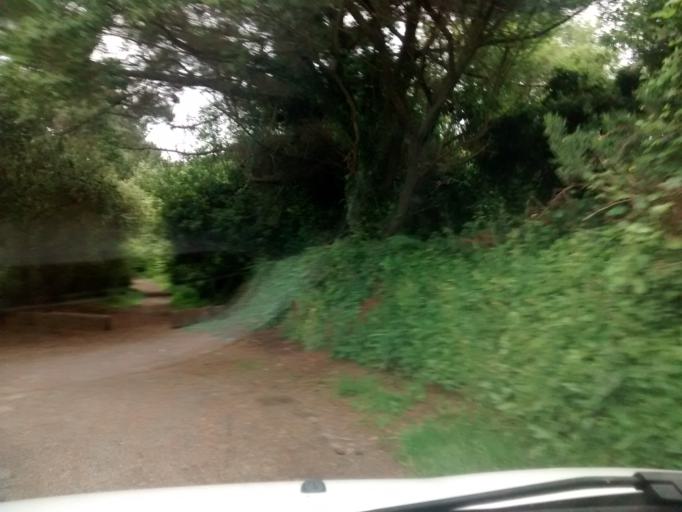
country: FR
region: Brittany
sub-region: Departement des Cotes-d'Armor
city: Tregastel
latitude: 48.8270
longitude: -3.4790
